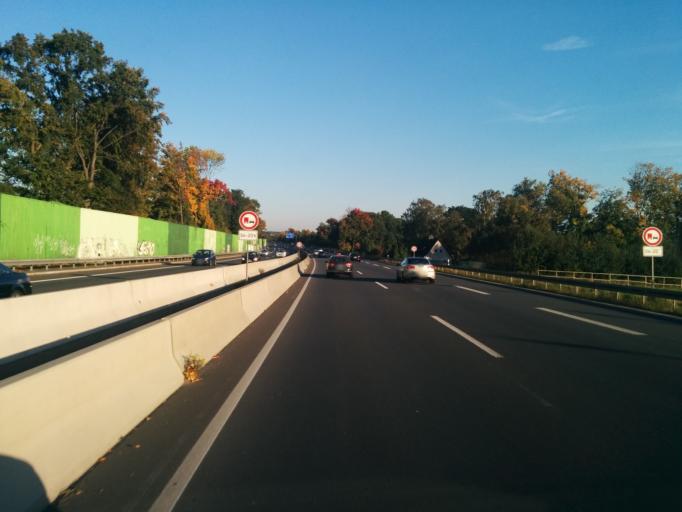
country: DE
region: North Rhine-Westphalia
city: Witten
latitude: 51.4937
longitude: 7.3441
